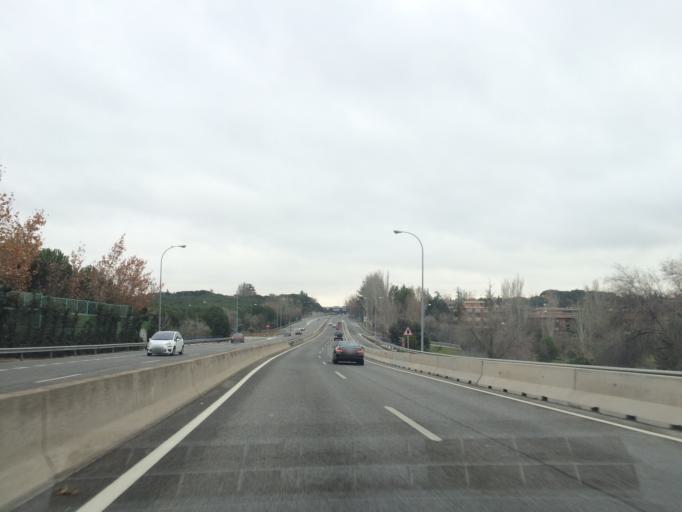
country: ES
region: Madrid
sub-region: Provincia de Madrid
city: Moncloa-Aravaca
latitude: 40.4548
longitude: -3.7667
